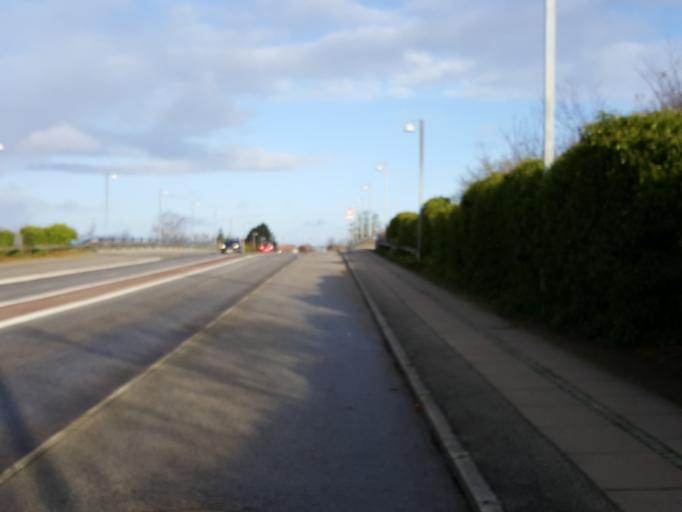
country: DK
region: Capital Region
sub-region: Tarnby Kommune
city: Tarnby
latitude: 55.6272
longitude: 12.5873
